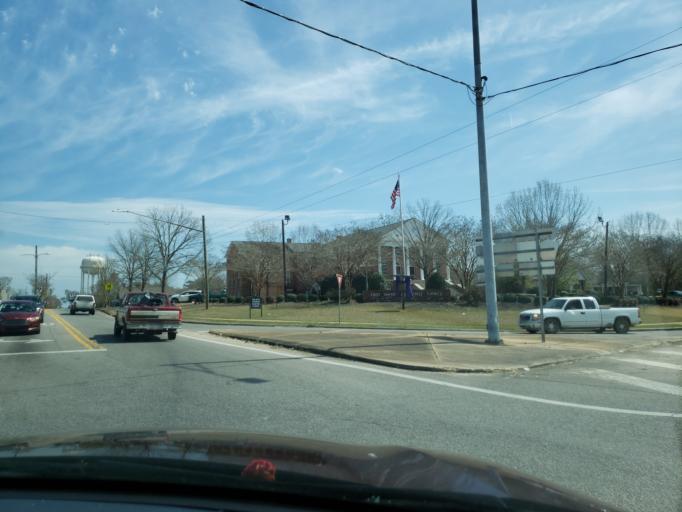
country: US
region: Alabama
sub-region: Elmore County
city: Tallassee
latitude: 32.5369
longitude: -85.8988
